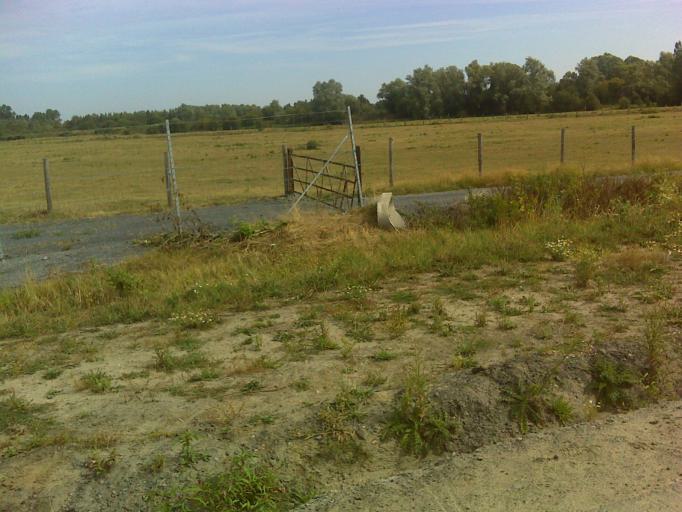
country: BE
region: Wallonia
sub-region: Province du Hainaut
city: Bernissart
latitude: 50.4505
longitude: 3.6493
